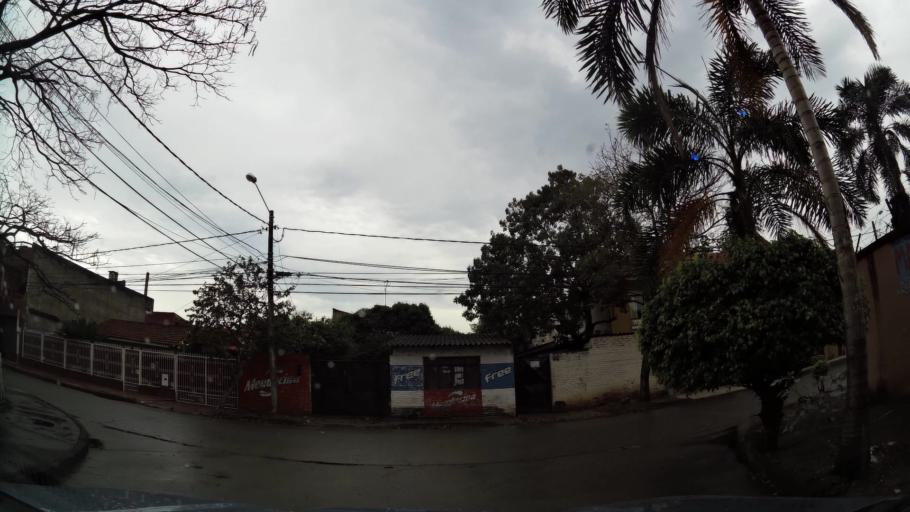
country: BO
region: Santa Cruz
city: Santa Cruz de la Sierra
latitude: -17.7651
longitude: -63.1573
